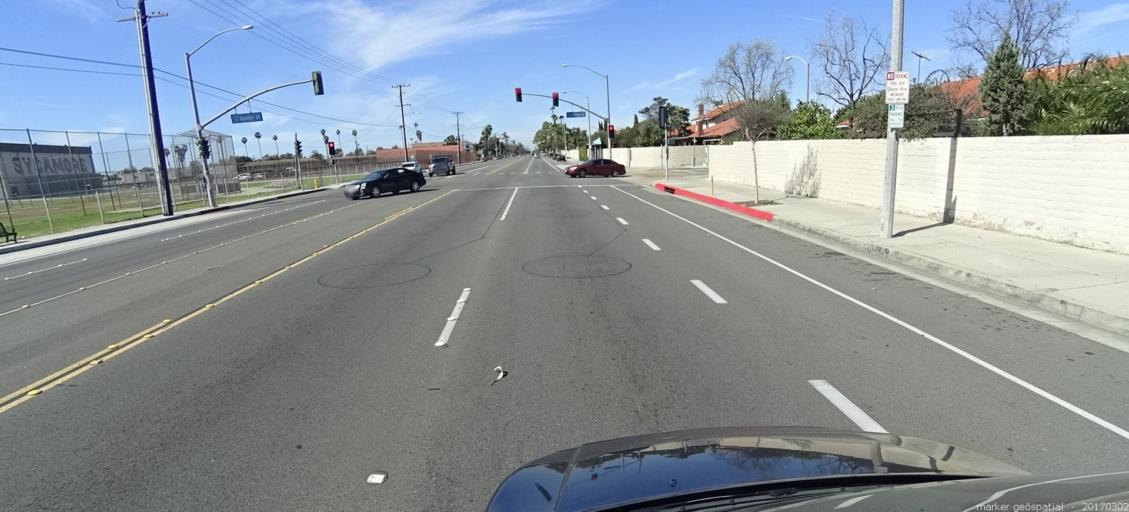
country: US
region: California
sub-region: Orange County
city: Anaheim
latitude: 33.8473
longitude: -117.8930
